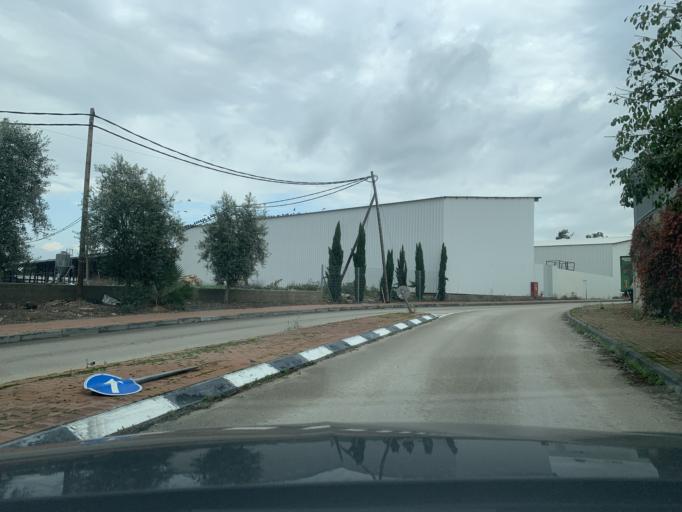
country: PS
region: West Bank
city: Qalqilyah
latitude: 32.2080
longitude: 34.9784
